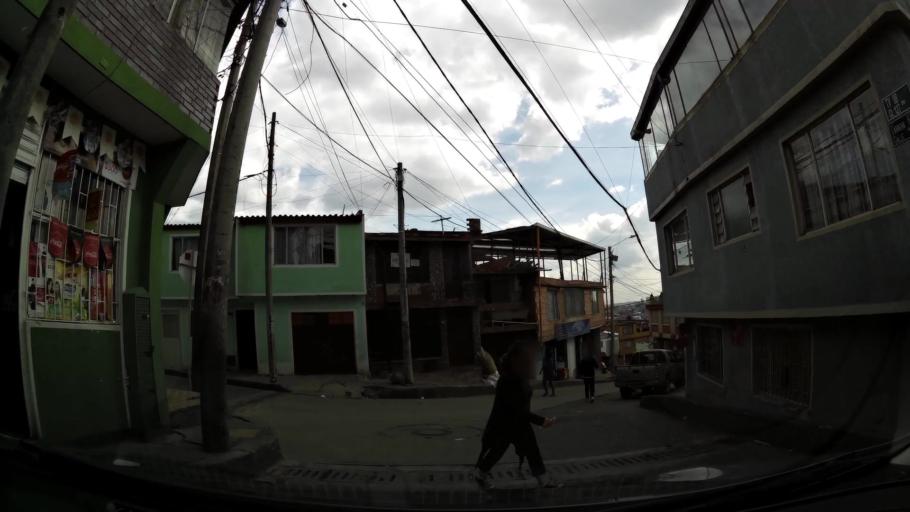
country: CO
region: Cundinamarca
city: Cota
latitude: 4.7263
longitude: -74.0857
